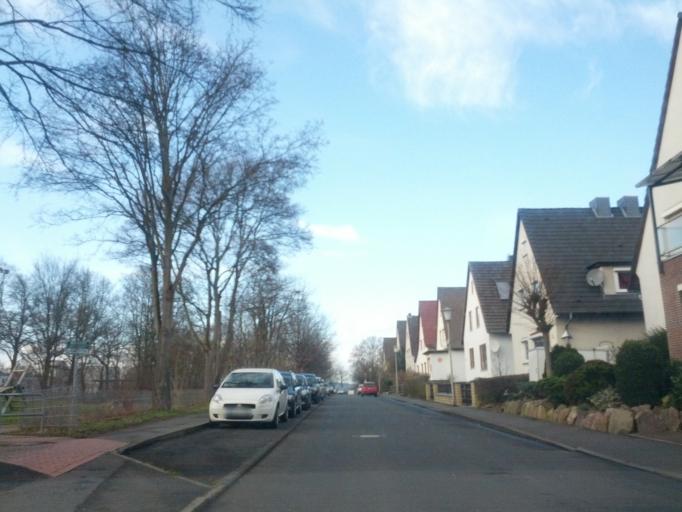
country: DE
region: Hesse
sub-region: Regierungsbezirk Kassel
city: Kassel
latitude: 51.3356
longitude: 9.5109
